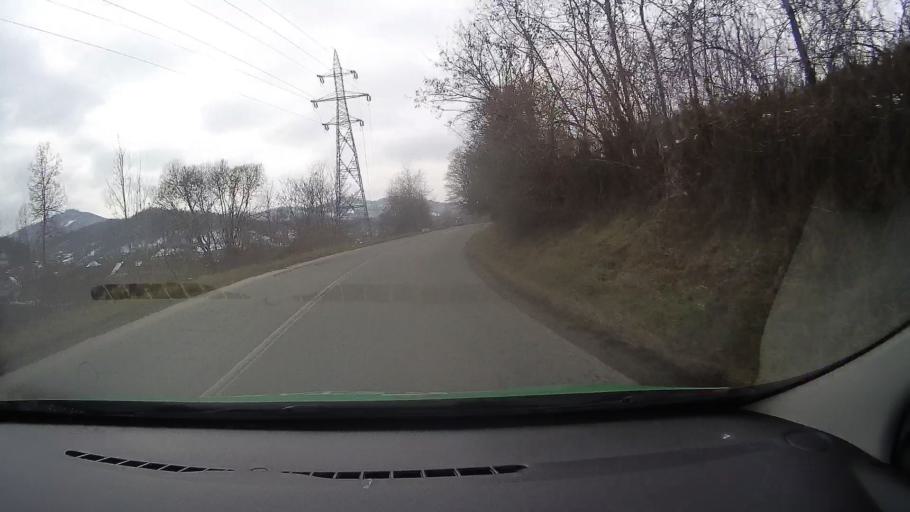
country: RO
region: Alba
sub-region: Oras Zlatna
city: Fenes
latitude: 46.0935
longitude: 23.2925
